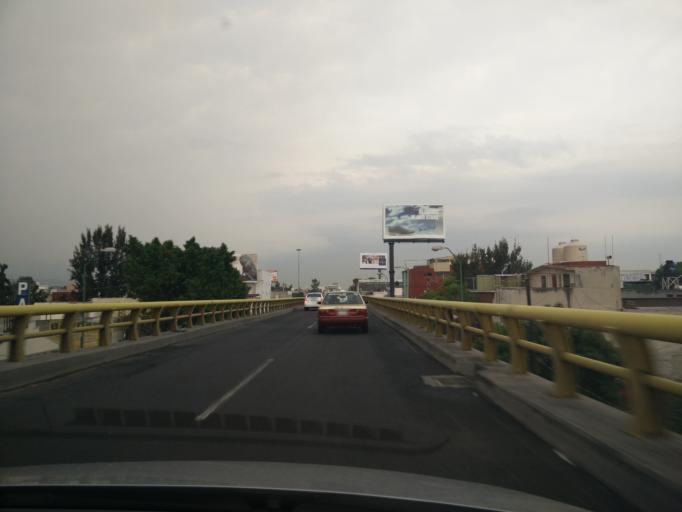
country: MX
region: Mexico City
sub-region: Iztacalco
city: Iztacalco
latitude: 19.4118
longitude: -99.0884
